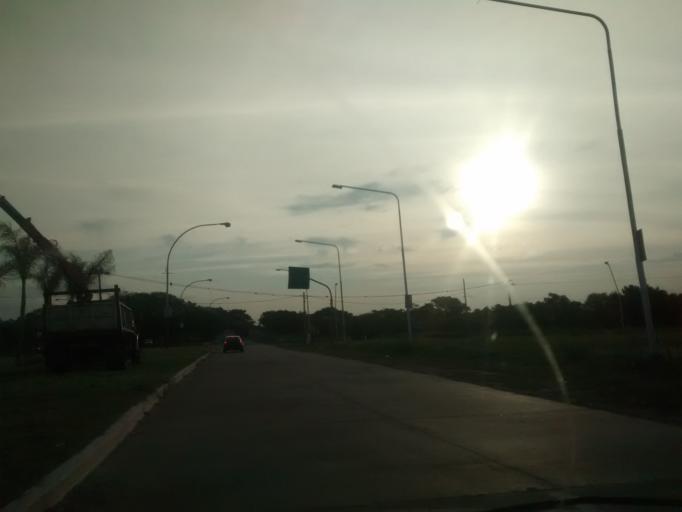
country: AR
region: Chaco
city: Resistencia
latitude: -27.4217
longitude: -58.9569
